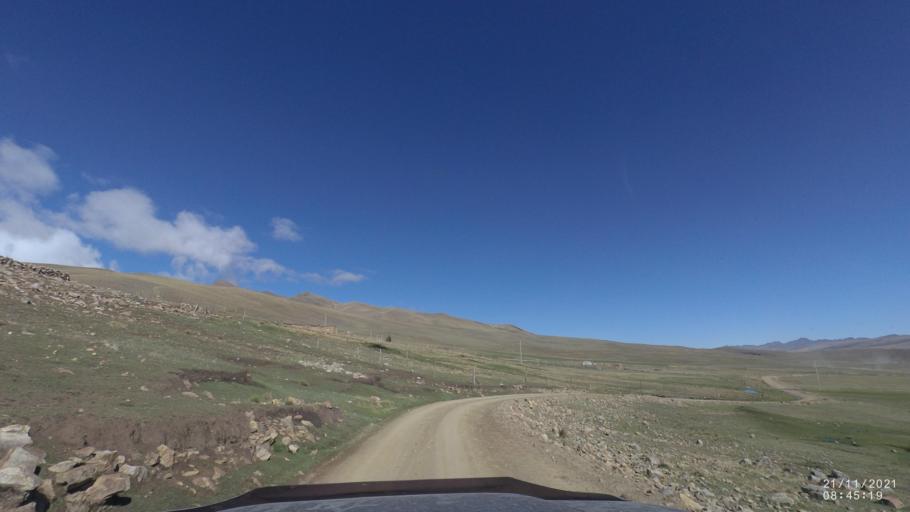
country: BO
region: Cochabamba
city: Cochabamba
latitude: -17.2494
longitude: -66.2315
